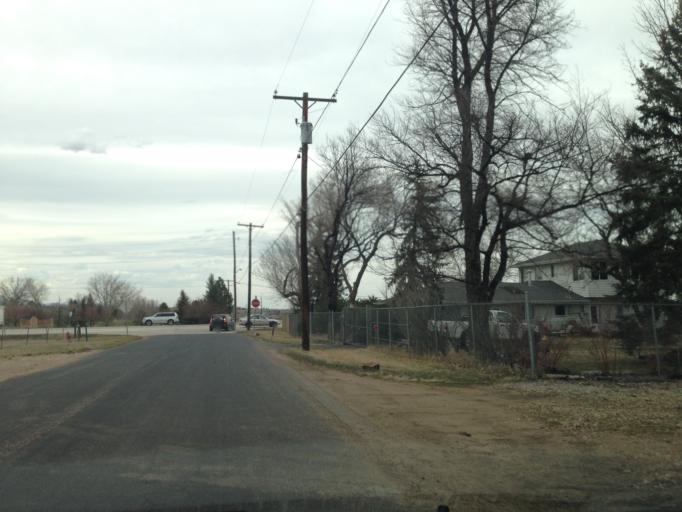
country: US
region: Colorado
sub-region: Boulder County
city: Superior
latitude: 39.9858
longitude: -105.1940
